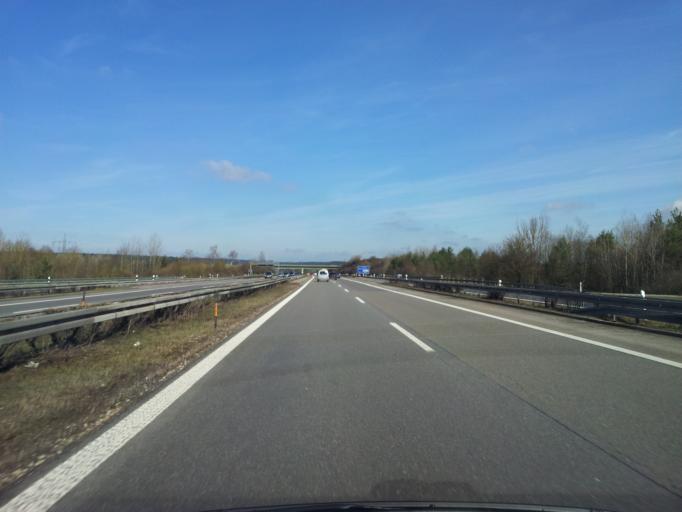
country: DE
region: Baden-Wuerttemberg
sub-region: Freiburg Region
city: Deisslingen
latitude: 48.0892
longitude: 8.5931
